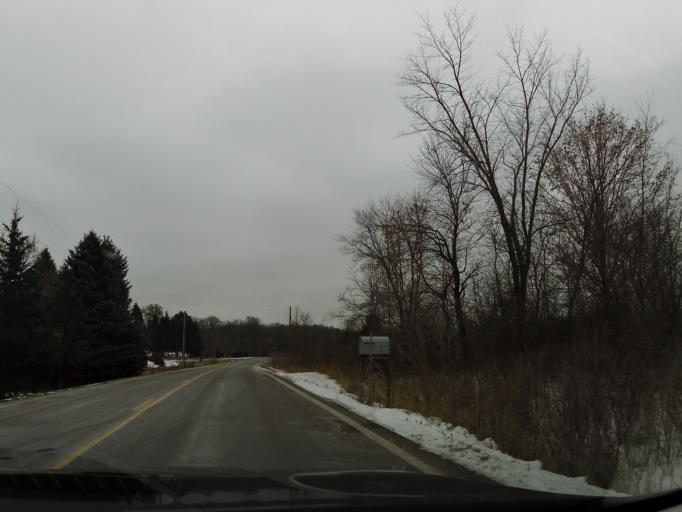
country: US
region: Minnesota
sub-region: Hennepin County
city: Medina
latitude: 45.0136
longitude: -93.6104
